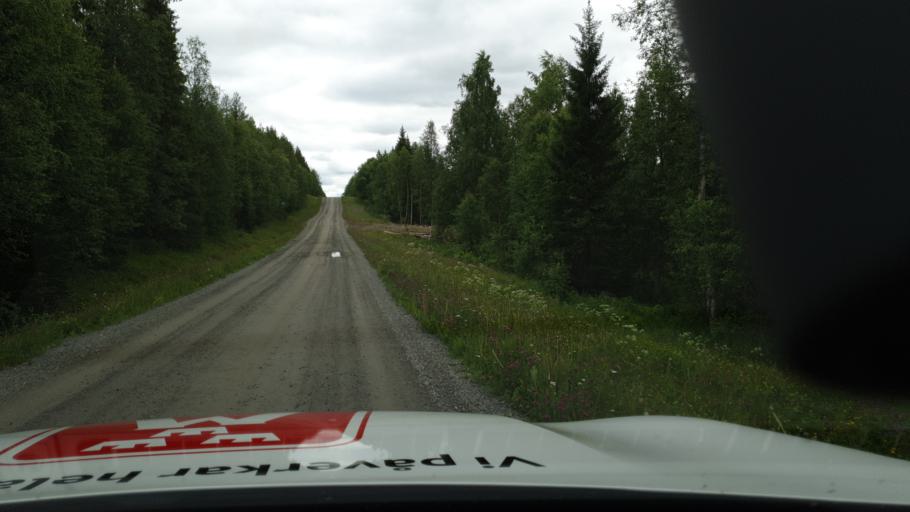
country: SE
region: Vaesterbotten
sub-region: Storumans Kommun
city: Storuman
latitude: 64.7795
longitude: 17.0344
